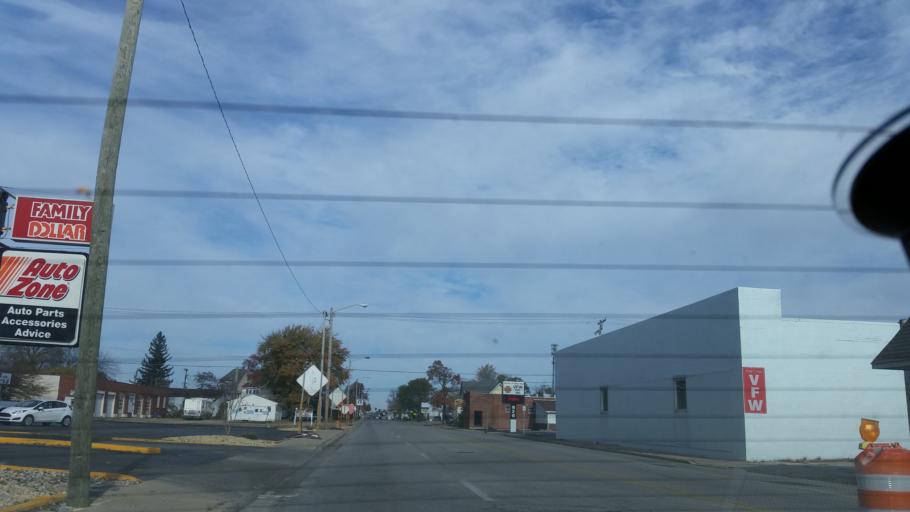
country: US
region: Indiana
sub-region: Howard County
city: Kokomo
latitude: 40.4937
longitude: -86.1338
